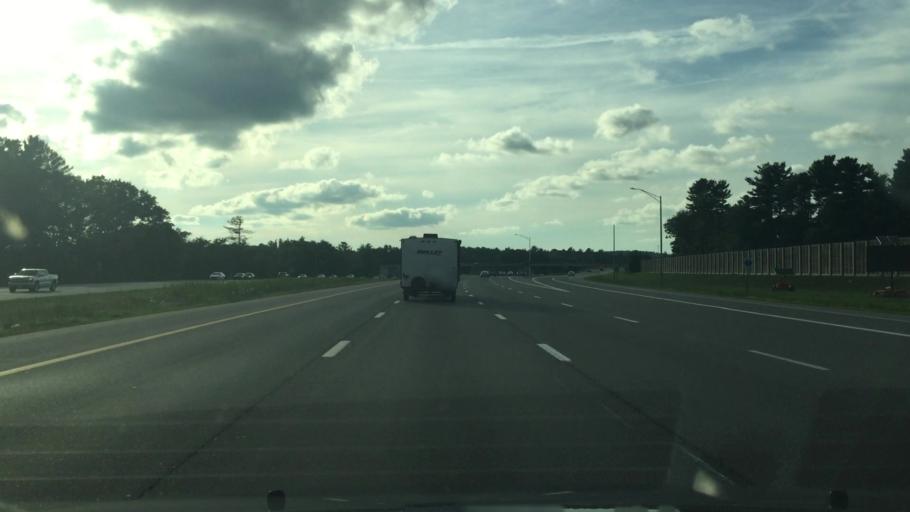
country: US
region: New Hampshire
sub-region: Rockingham County
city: Salem
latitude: 42.7572
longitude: -71.2279
